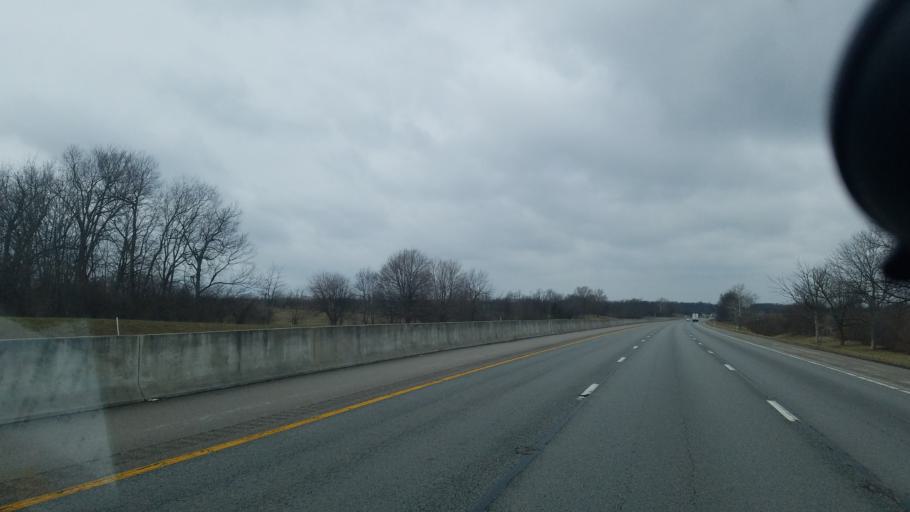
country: US
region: Kentucky
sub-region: Clark County
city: Winchester
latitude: 38.0370
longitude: -84.2886
